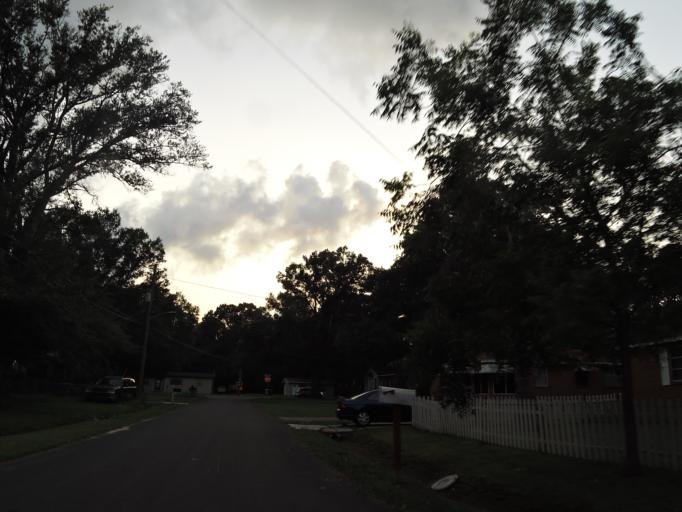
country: US
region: Florida
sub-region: Duval County
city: Jacksonville
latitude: 30.3309
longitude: -81.7259
